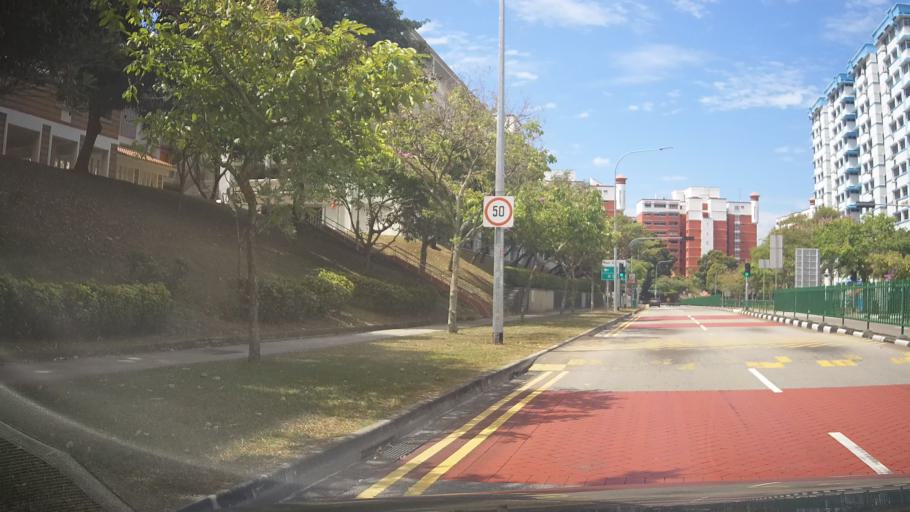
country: SG
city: Singapore
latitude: 1.3649
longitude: 103.9620
